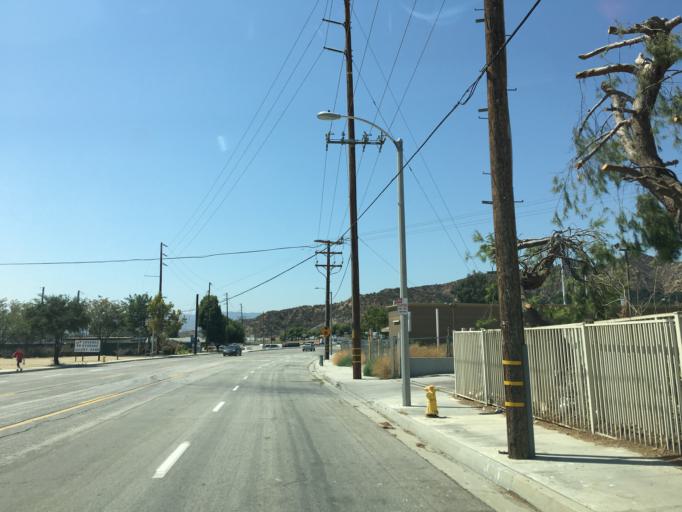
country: US
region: California
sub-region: Los Angeles County
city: Castaic
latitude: 34.4926
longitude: -118.6168
